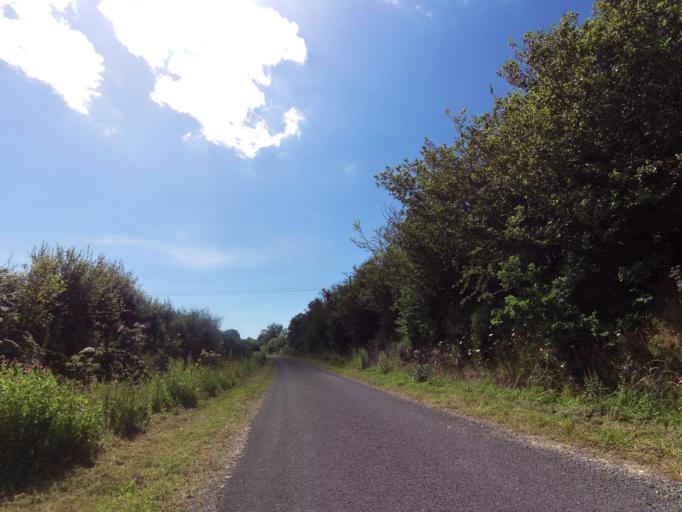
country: IE
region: Munster
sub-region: Waterford
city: Portlaw
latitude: 52.2370
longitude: -7.2999
